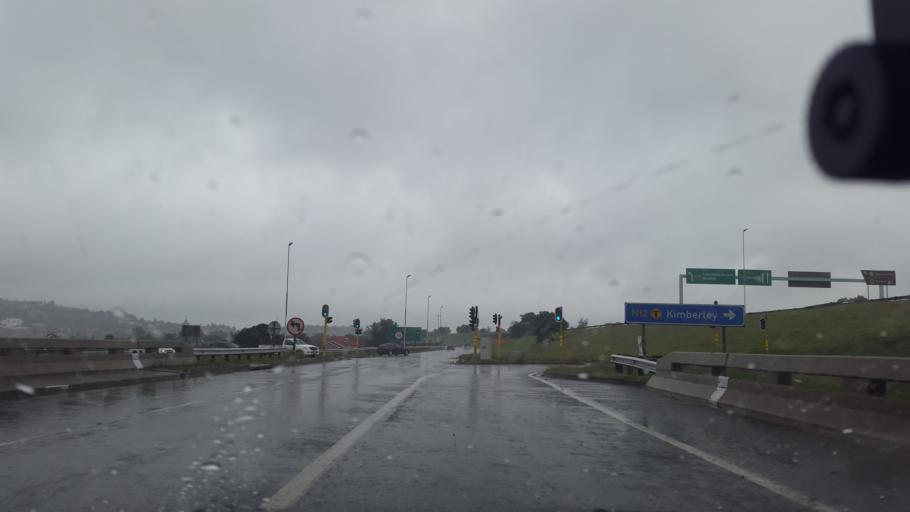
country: ZA
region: Gauteng
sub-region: City of Johannesburg Metropolitan Municipality
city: Johannesburg
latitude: -26.2670
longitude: 28.0318
